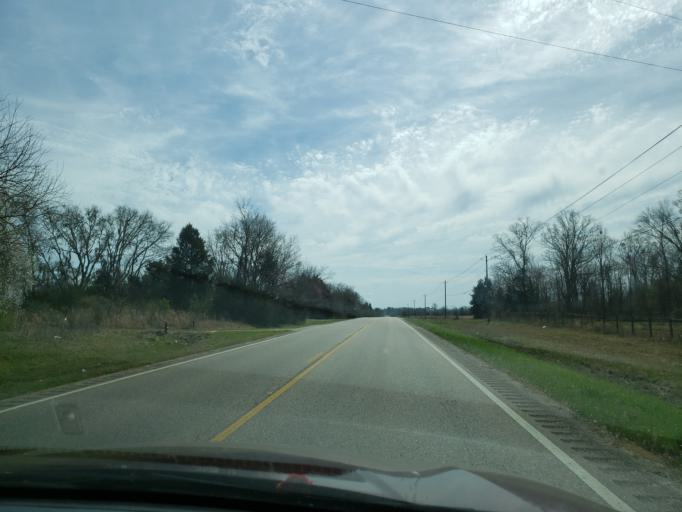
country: US
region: Alabama
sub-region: Dallas County
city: Selma
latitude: 32.4444
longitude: -87.0713
